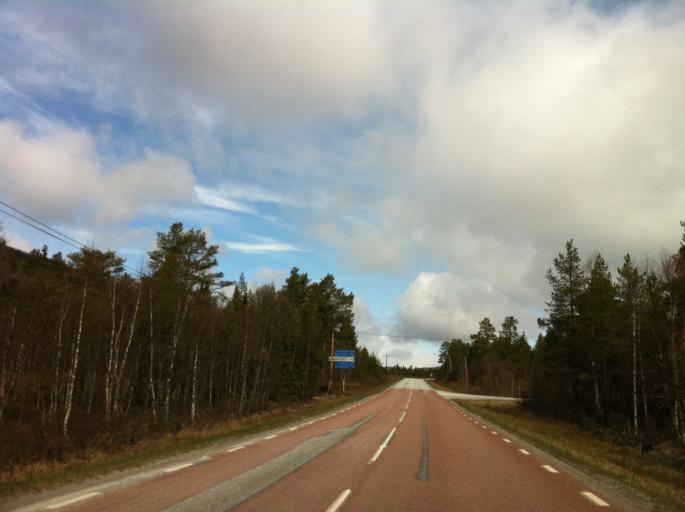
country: SE
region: Jaemtland
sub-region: Are Kommun
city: Are
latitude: 62.5555
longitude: 12.5679
